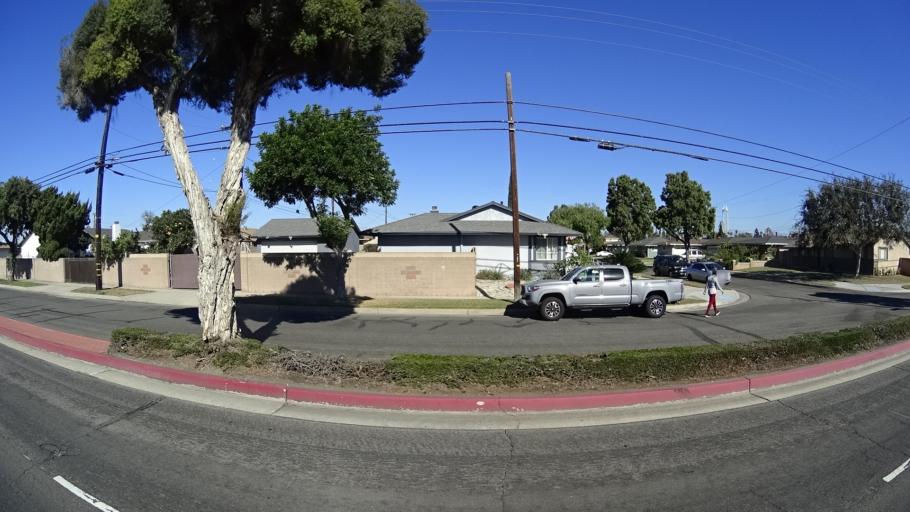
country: US
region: California
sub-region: Orange County
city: Buena Park
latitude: 33.8393
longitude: -118.0056
